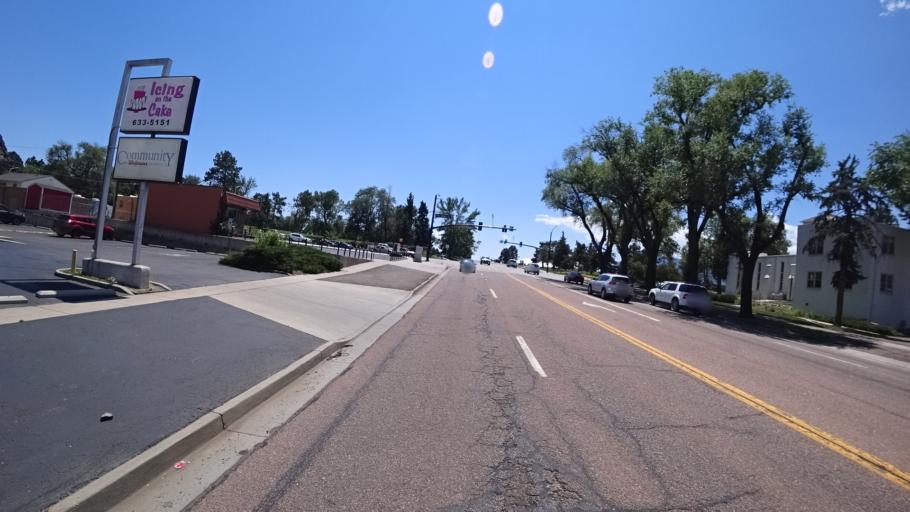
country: US
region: Colorado
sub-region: El Paso County
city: Colorado Springs
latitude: 38.8335
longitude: -104.7946
